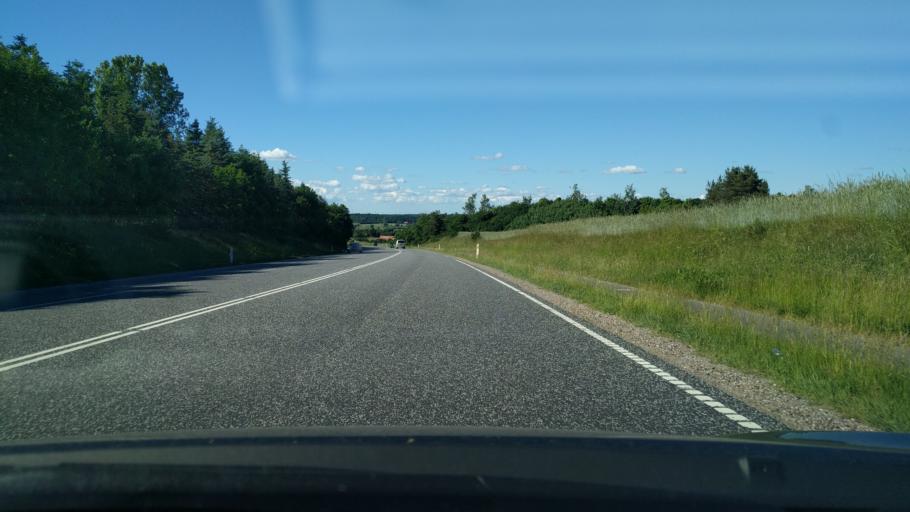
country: DK
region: Central Jutland
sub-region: Viborg Kommune
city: Viborg
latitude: 56.5588
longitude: 9.4838
